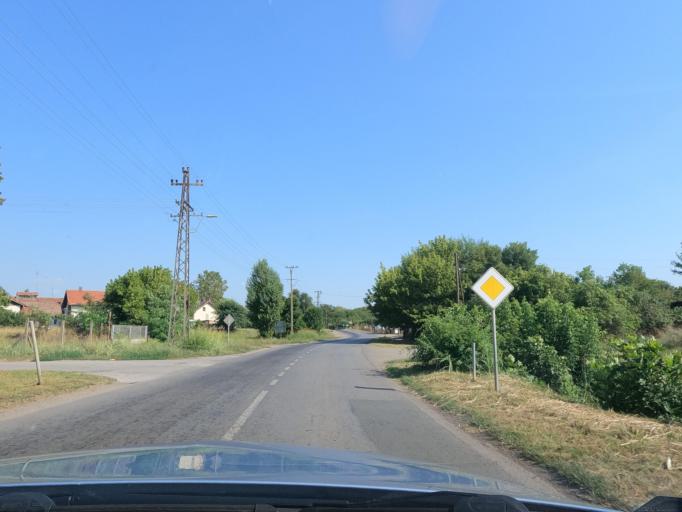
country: RS
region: Autonomna Pokrajina Vojvodina
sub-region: Juznobacki Okrug
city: Becej
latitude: 45.6230
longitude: 20.0332
